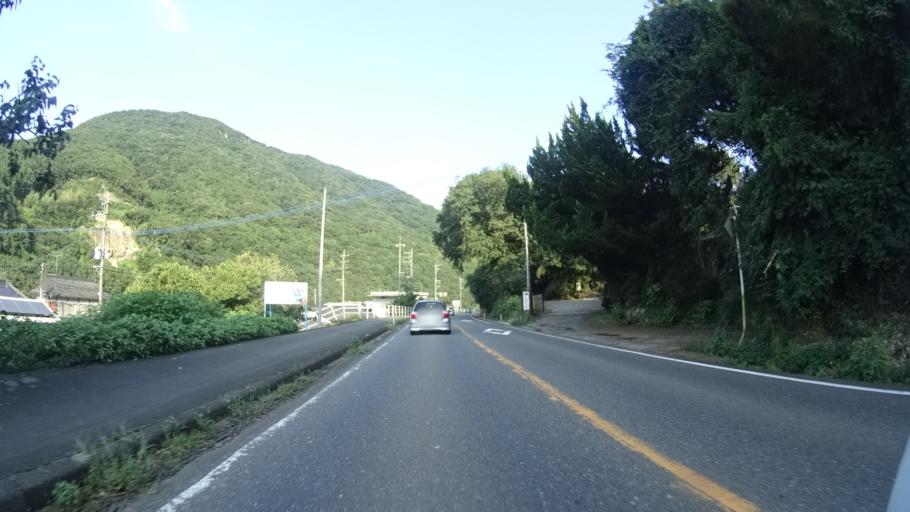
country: JP
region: Oita
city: Bungo-Takada-shi
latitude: 33.4903
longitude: 131.3304
